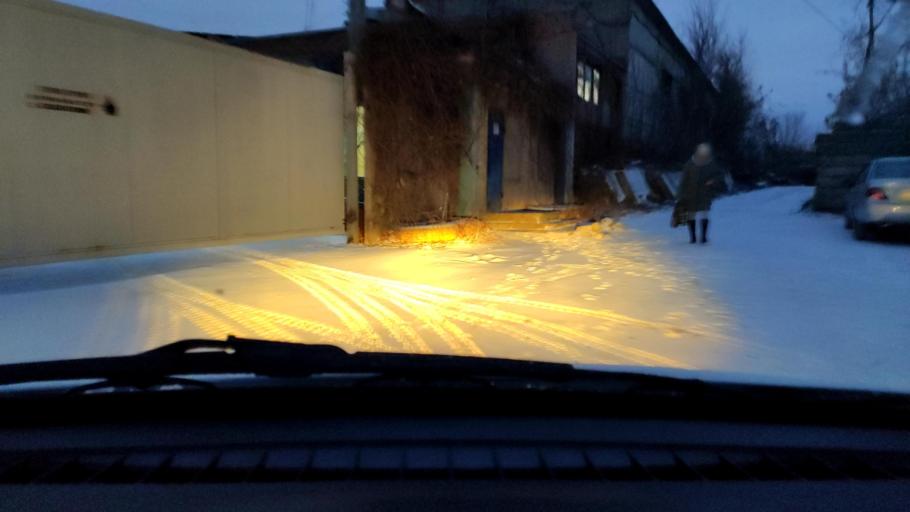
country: RU
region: Voronezj
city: Voronezh
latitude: 51.6858
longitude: 39.1463
